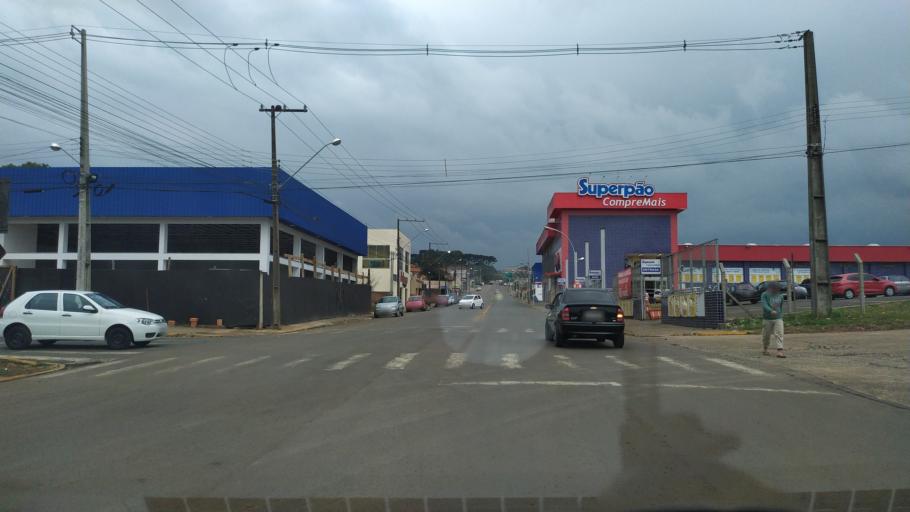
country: BR
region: Parana
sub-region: Palmas
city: Palmas
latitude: -26.4891
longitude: -51.9982
